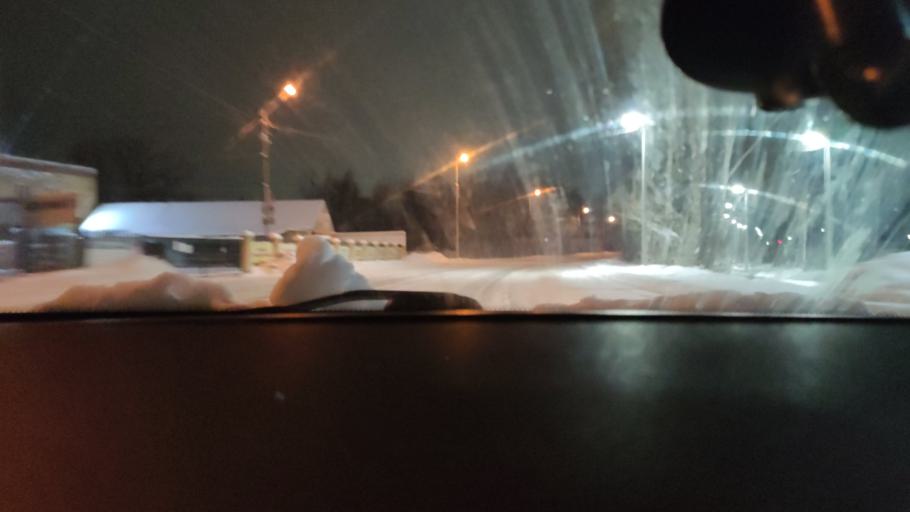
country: RU
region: Perm
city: Krasnokamsk
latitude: 58.0623
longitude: 55.8023
